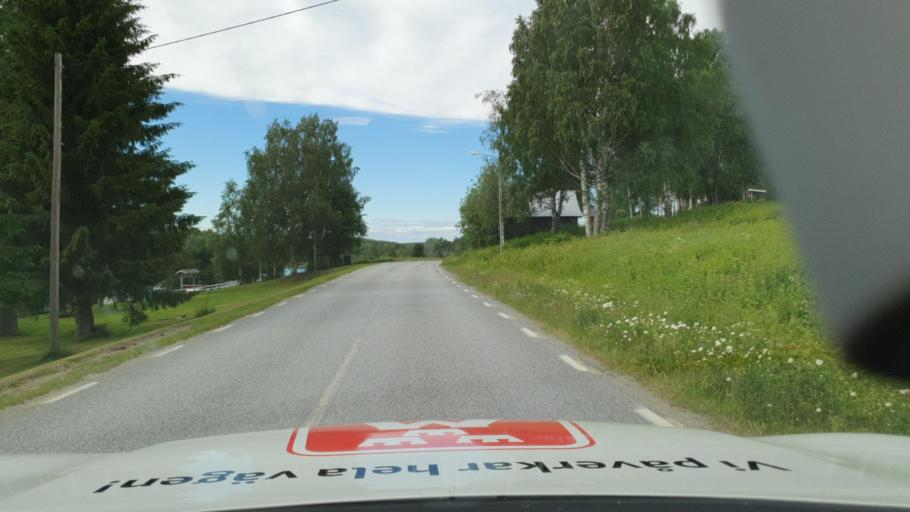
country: SE
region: Vaesterbotten
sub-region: Skelleftea Kommun
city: Burea
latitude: 64.4935
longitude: 21.0229
